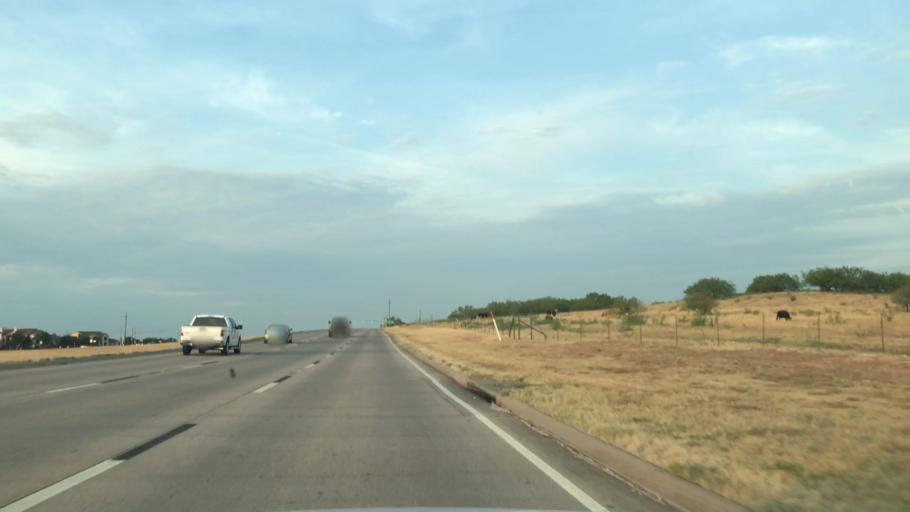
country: US
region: Texas
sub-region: Tarrant County
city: Keller
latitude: 32.9689
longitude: -97.2858
